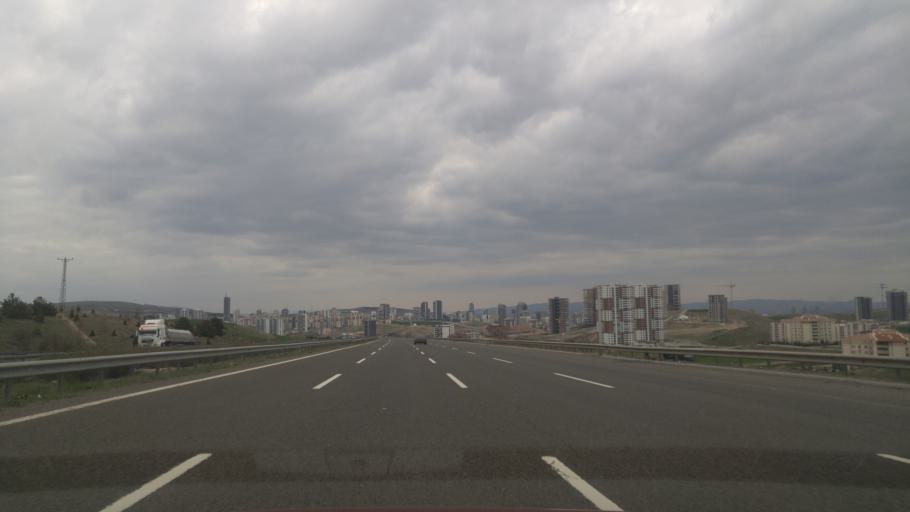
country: TR
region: Ankara
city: Etimesgut
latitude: 39.8271
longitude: 32.6462
